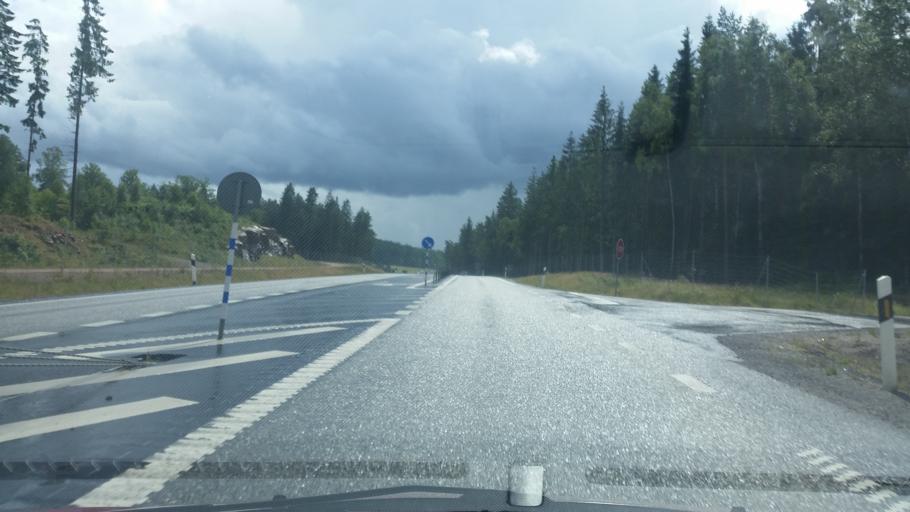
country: SE
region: Joenkoeping
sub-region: Gislaveds Kommun
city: Reftele
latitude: 57.2571
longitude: 13.6348
